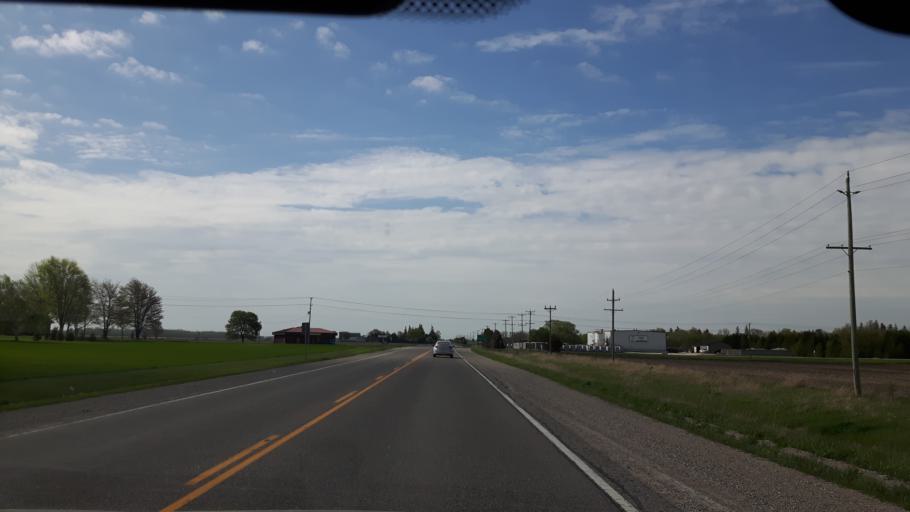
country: CA
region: Ontario
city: South Huron
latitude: 43.2911
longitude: -81.4694
